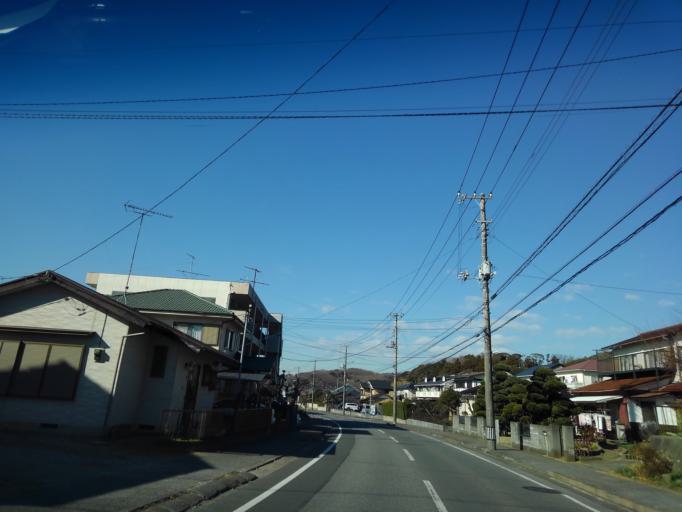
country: JP
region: Chiba
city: Kimitsu
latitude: 35.3343
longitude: 139.9201
